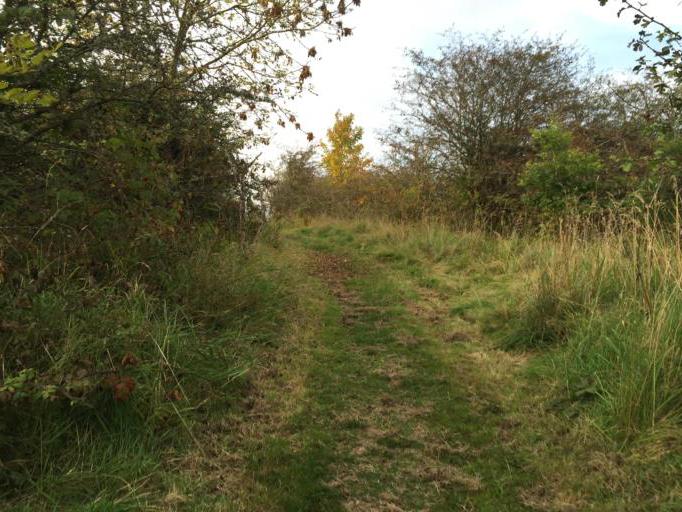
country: GB
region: Scotland
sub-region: West Lothian
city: Livingston
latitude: 55.9326
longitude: -3.5125
